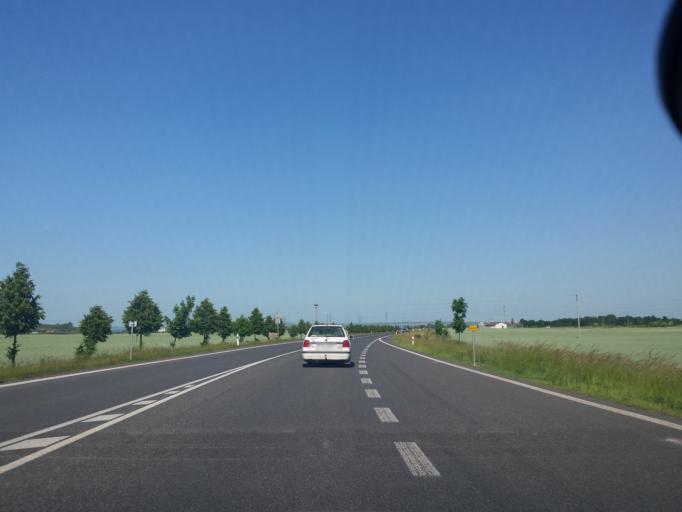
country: CZ
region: Central Bohemia
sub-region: Okres Melnik
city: Veltrusy
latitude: 50.3240
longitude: 14.3410
